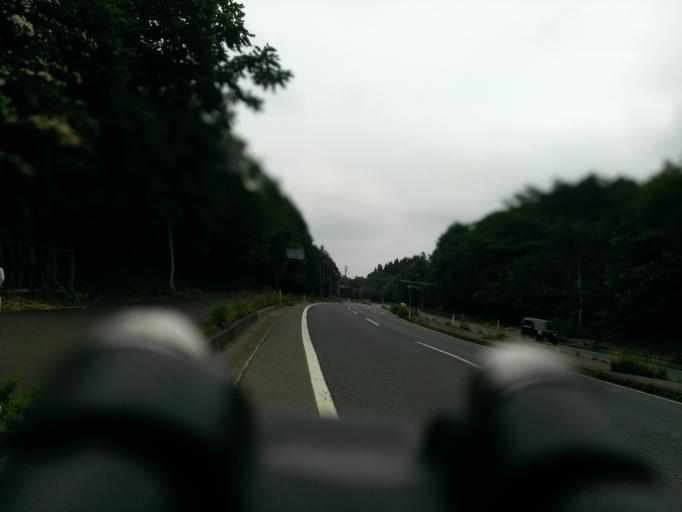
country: JP
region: Iwate
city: Morioka-shi
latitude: 39.8025
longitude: 141.1233
